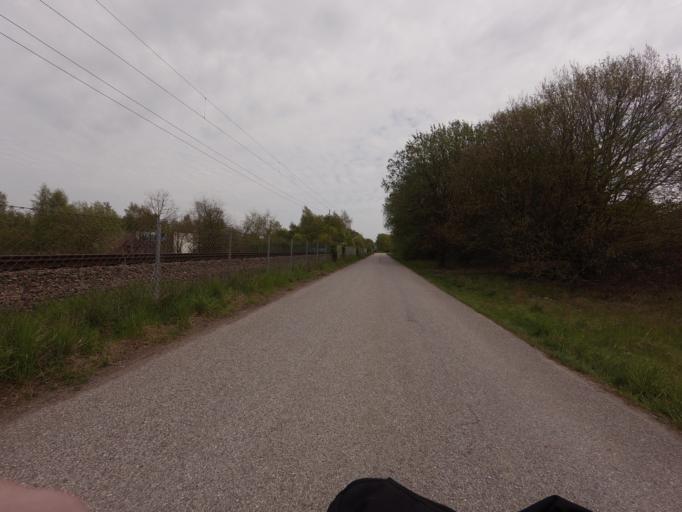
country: SE
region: Skane
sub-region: Malmo
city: Oxie
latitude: 55.5431
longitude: 13.0897
